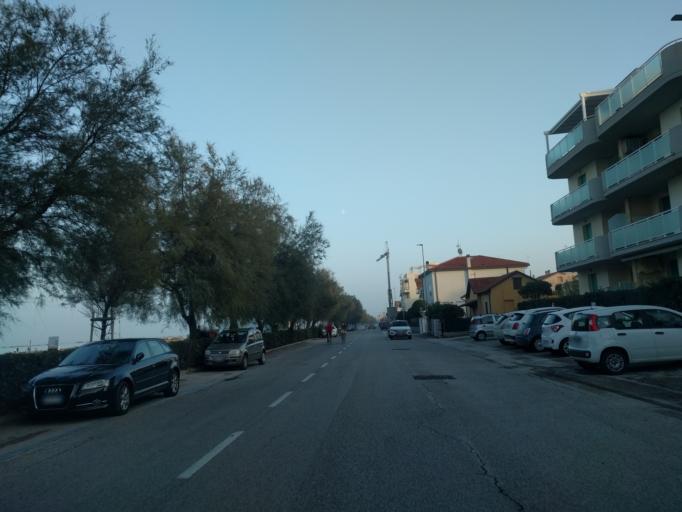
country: IT
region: The Marches
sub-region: Provincia di Ancona
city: Senigallia
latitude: 43.7357
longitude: 13.1930
